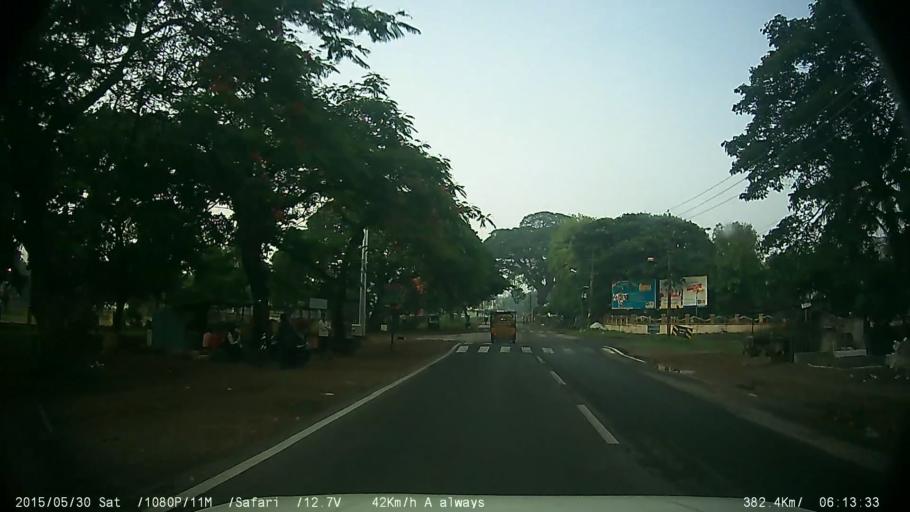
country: IN
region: Karnataka
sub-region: Mysore
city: Mysore
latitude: 12.3333
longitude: 76.6578
